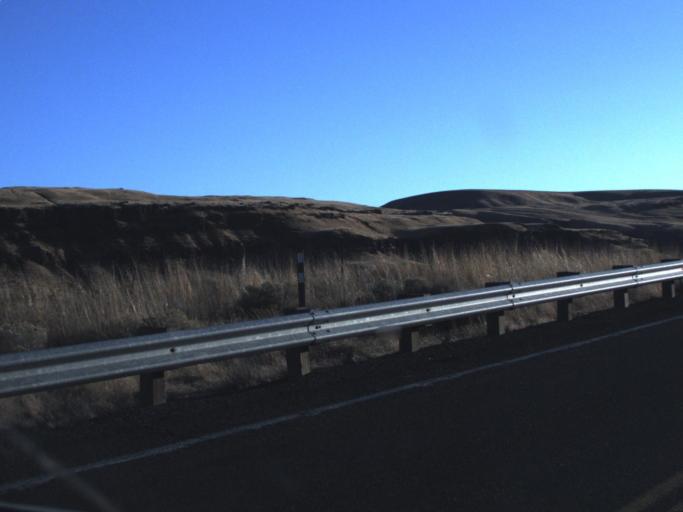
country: US
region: Washington
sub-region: Franklin County
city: Connell
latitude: 46.6518
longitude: -118.4995
